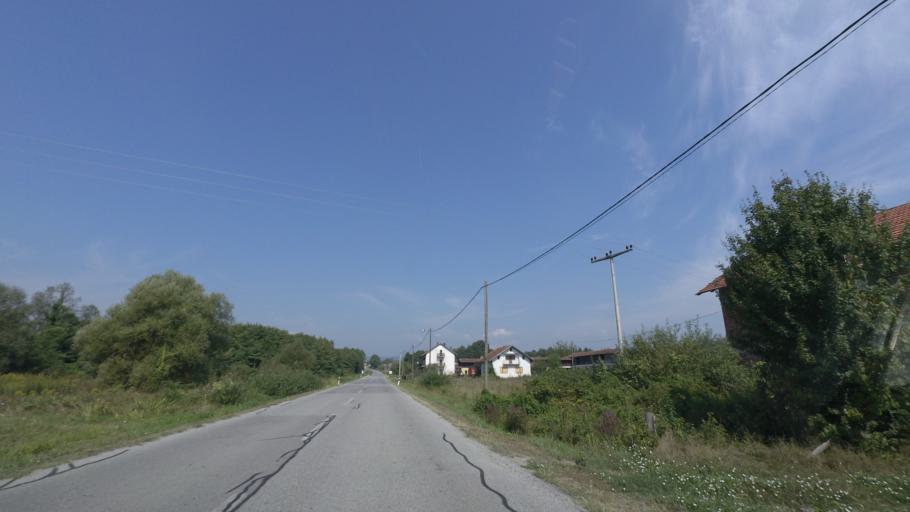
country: HR
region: Sisacko-Moslavacka
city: Dvor
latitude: 45.0969
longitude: 16.2947
